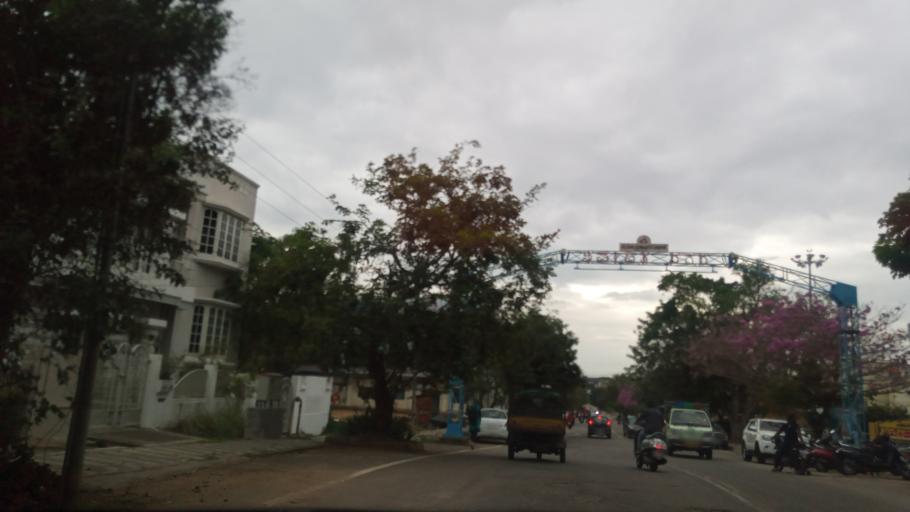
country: IN
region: Karnataka
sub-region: Mysore
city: Mysore
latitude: 12.2953
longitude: 76.6109
